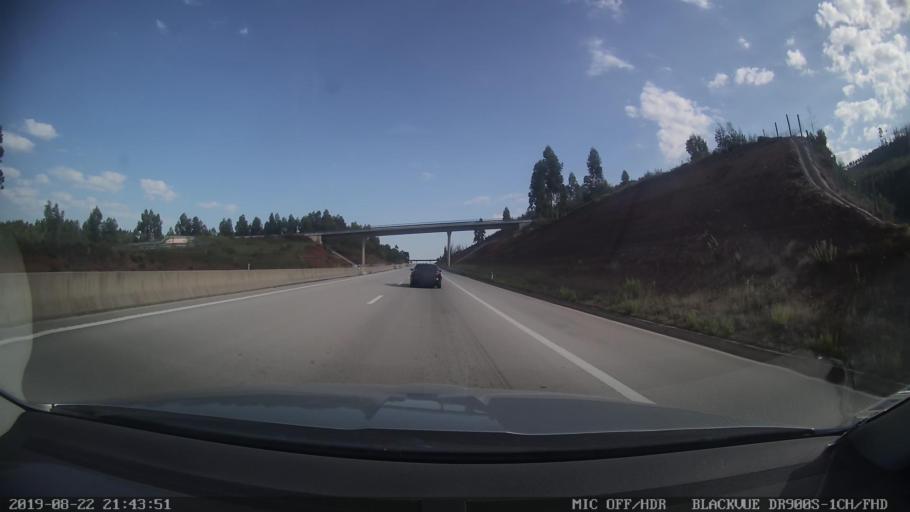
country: PT
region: Leiria
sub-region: Figueiro Dos Vinhos
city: Figueiro dos Vinhos
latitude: 39.9411
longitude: -8.3476
